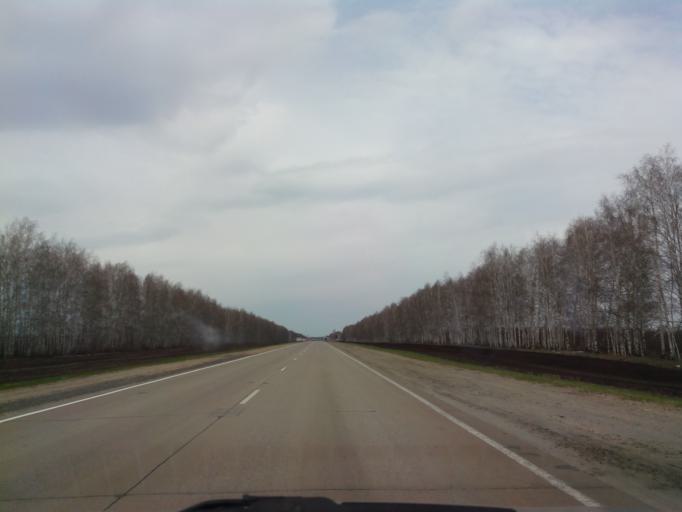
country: RU
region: Tambov
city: Satinka
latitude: 52.2190
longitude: 41.5529
